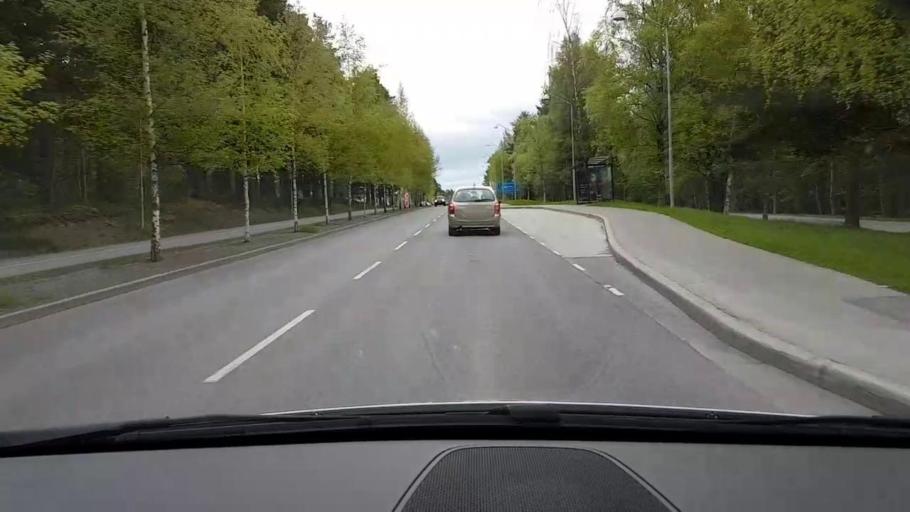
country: SE
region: Jaemtland
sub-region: OEstersunds Kommun
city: Ostersund
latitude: 63.1603
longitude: 14.6661
